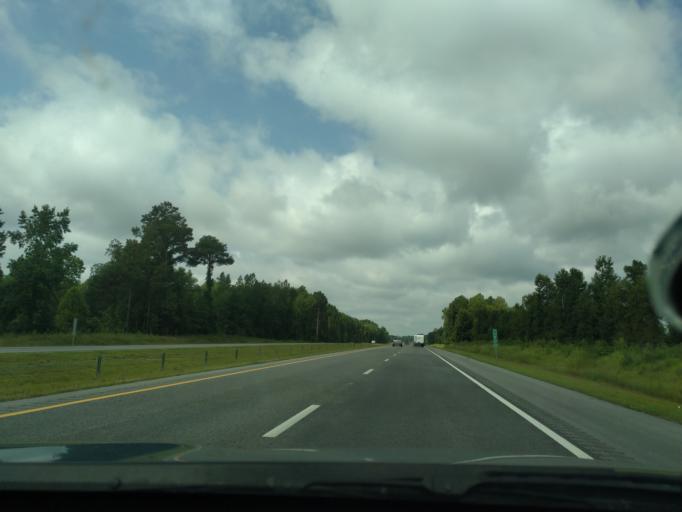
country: US
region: North Carolina
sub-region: Martin County
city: Robersonville
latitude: 35.8328
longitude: -77.2991
